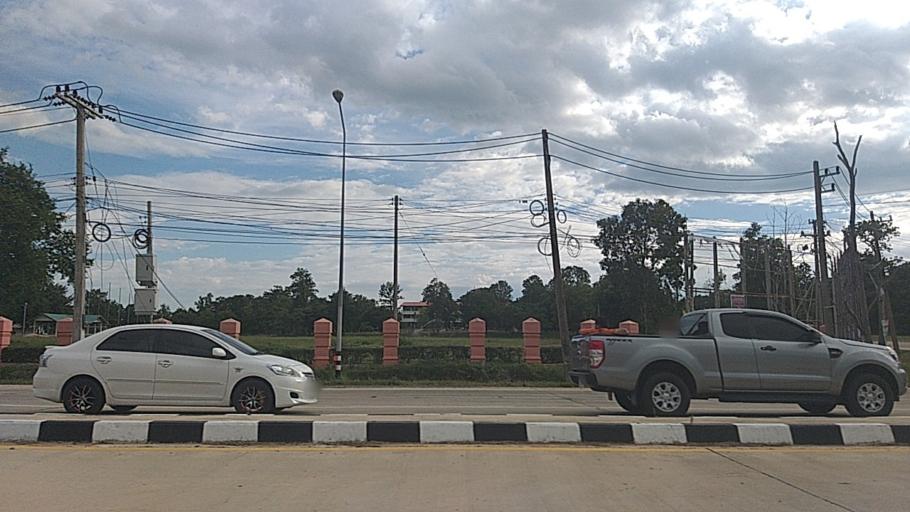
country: TH
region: Surin
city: Kap Choeng
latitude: 14.5475
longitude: 103.5129
